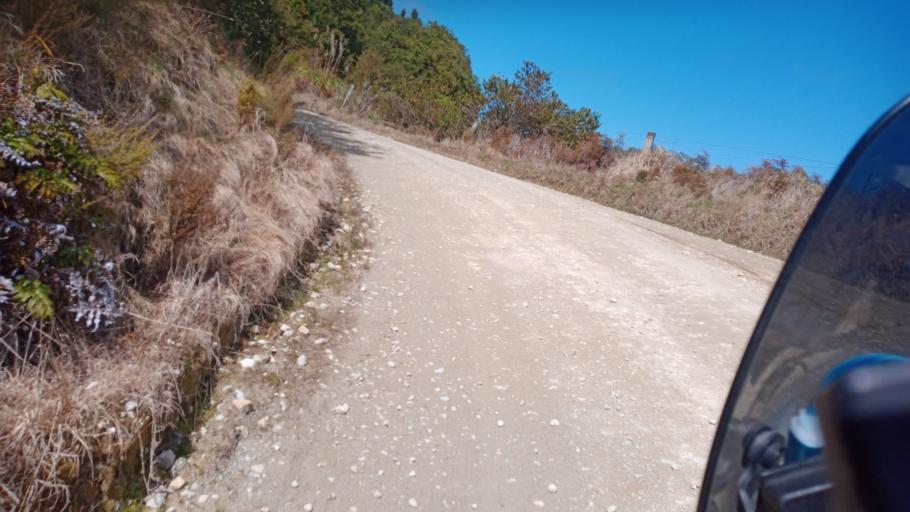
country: NZ
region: Gisborne
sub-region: Gisborne District
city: Gisborne
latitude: -38.8538
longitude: 177.7909
